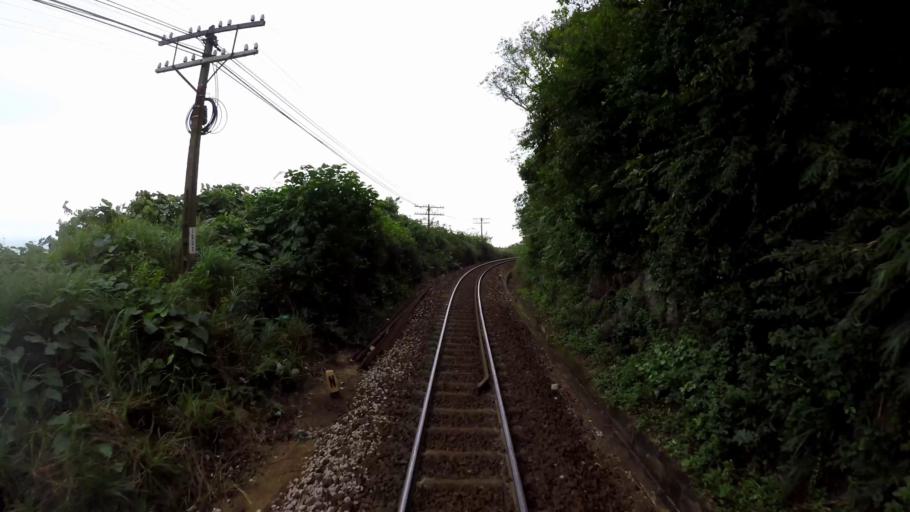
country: VN
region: Da Nang
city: Lien Chieu
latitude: 16.2142
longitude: 108.1299
